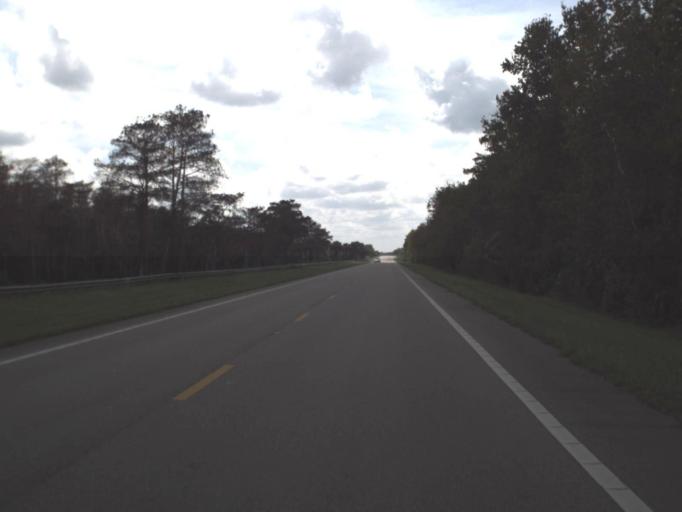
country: US
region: Florida
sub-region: Collier County
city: Immokalee
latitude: 26.2288
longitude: -81.3439
